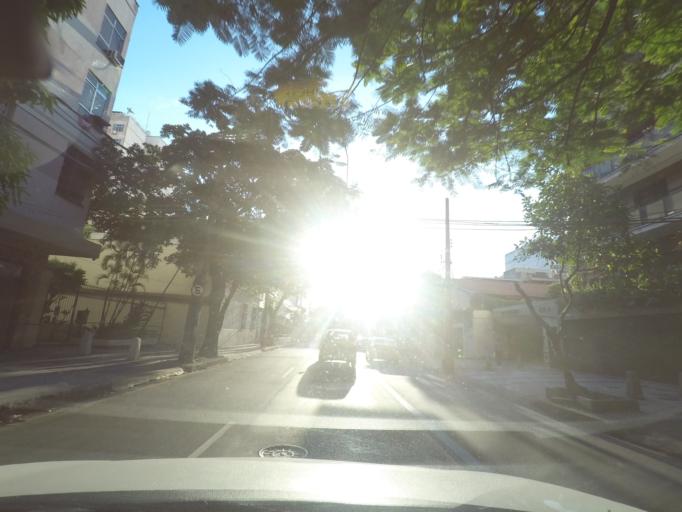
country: BR
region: Rio de Janeiro
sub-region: Rio De Janeiro
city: Rio de Janeiro
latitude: -22.9188
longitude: -43.2187
